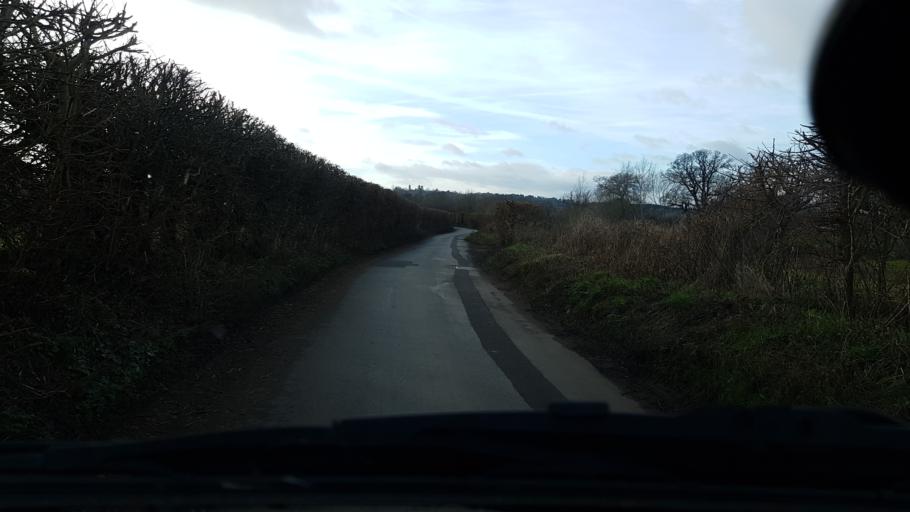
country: GB
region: England
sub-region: Surrey
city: Cobham
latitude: 51.3214
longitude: -0.4139
